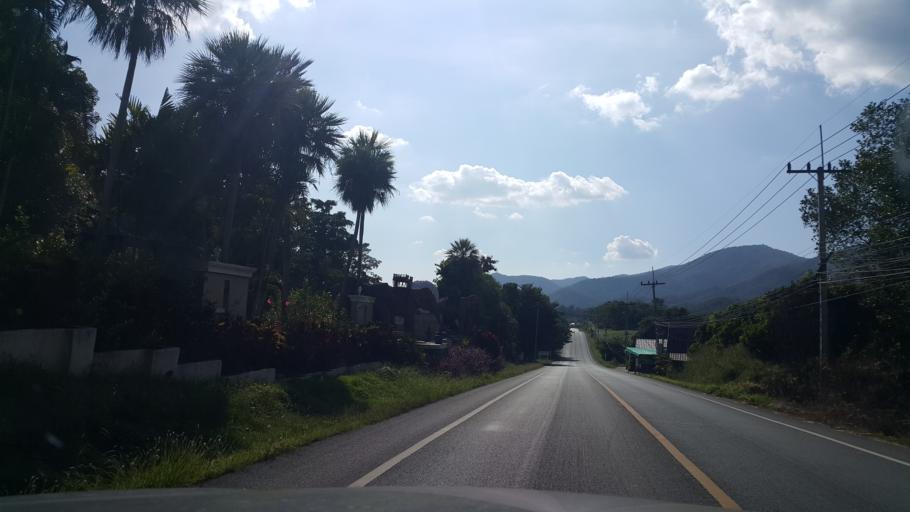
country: TH
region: Lamphun
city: Mae Tha
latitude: 18.5207
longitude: 99.2269
